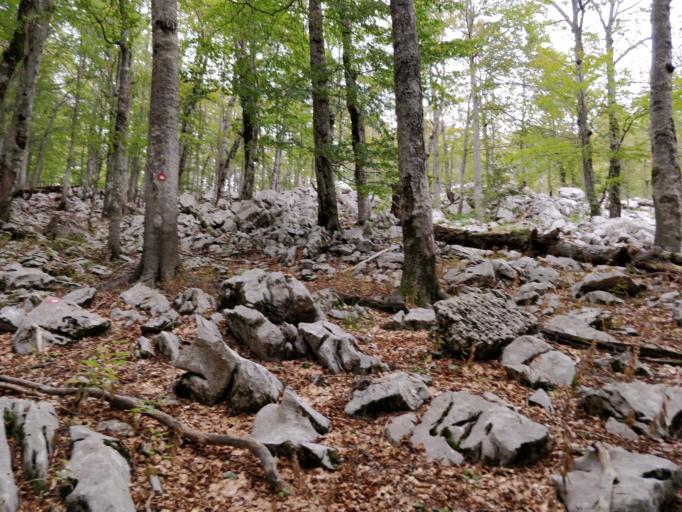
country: HR
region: Zadarska
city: Starigrad
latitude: 44.3843
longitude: 15.4893
